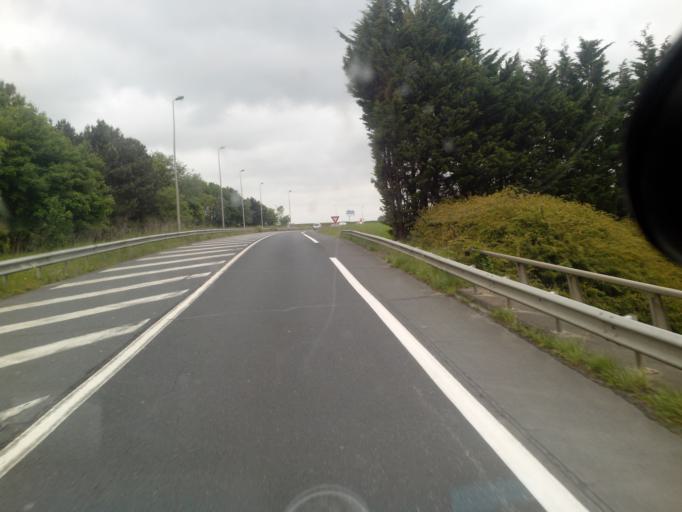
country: FR
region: Lower Normandy
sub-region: Departement du Calvados
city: Saint-Germain-la-Blanche-Herbe
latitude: 49.1896
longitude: -0.4219
